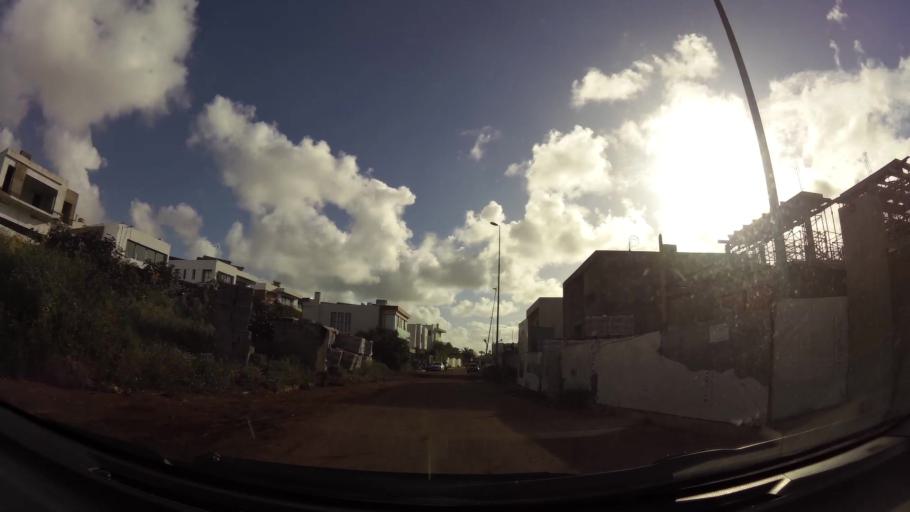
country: MA
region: Grand Casablanca
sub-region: Casablanca
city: Casablanca
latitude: 33.5755
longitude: -7.6887
